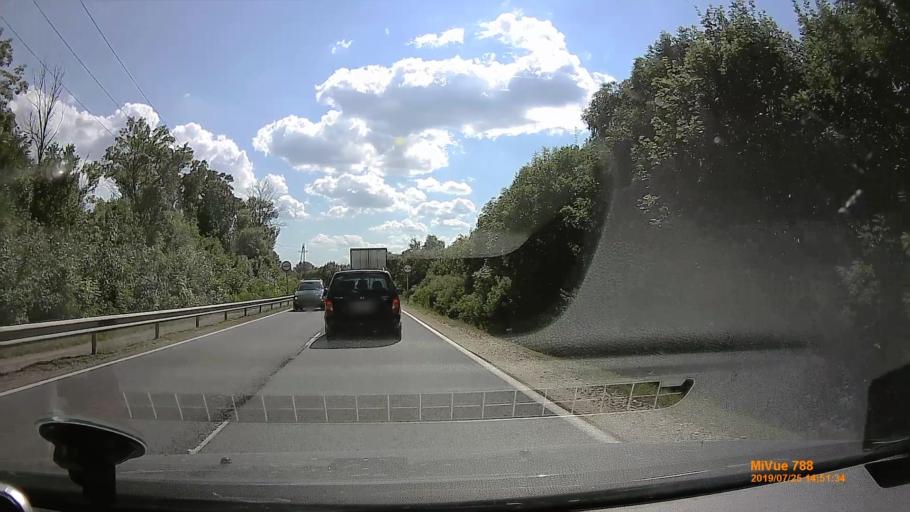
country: HU
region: Borsod-Abauj-Zemplen
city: Szikszo
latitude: 48.2137
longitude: 20.9417
